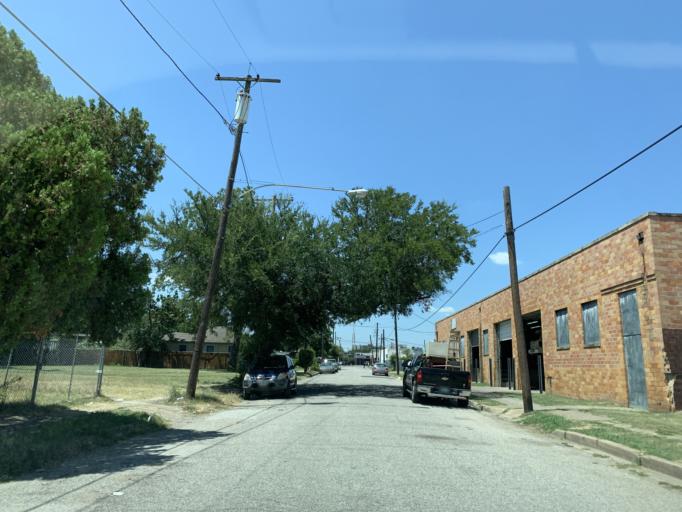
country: US
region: Texas
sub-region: Dallas County
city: Dallas
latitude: 32.7743
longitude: -96.7660
